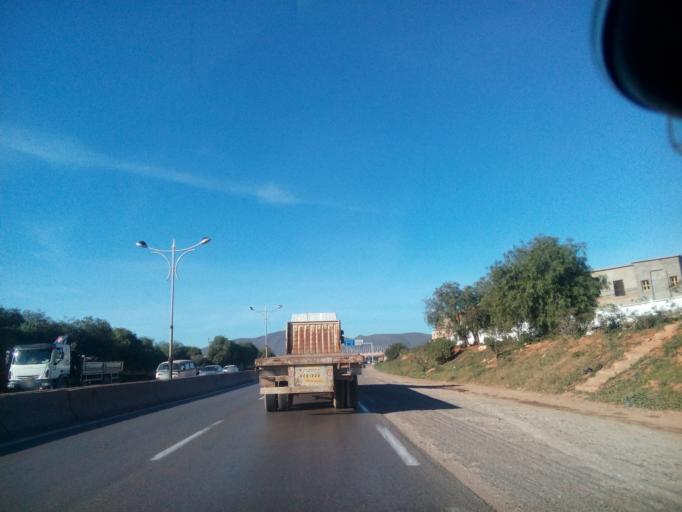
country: DZ
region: Oran
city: Bir el Djir
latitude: 35.7734
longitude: -0.4312
